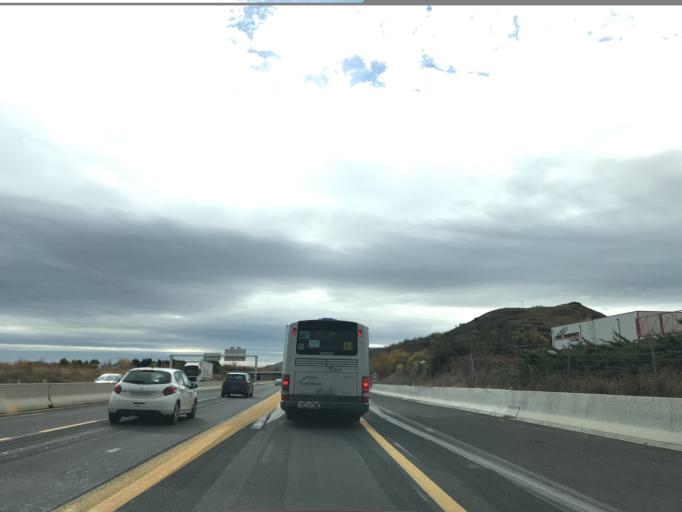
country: FR
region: Auvergne
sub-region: Departement du Puy-de-Dome
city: Aulnat
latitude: 45.7785
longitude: 3.1409
